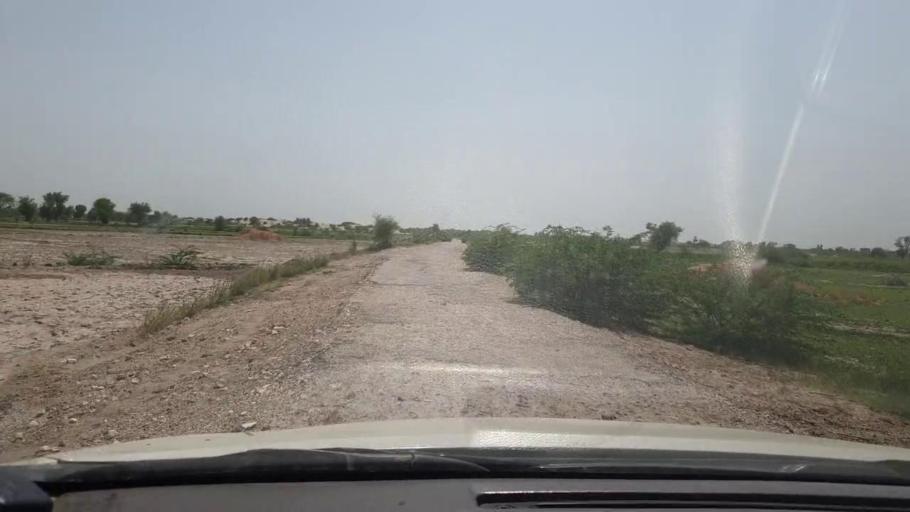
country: PK
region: Sindh
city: Rohri
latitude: 27.5230
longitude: 69.1017
